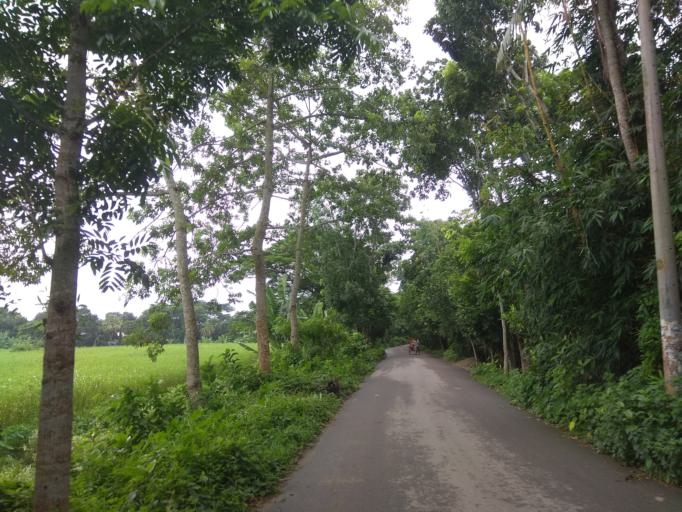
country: BD
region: Dhaka
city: Dohar
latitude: 23.4197
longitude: 90.0687
